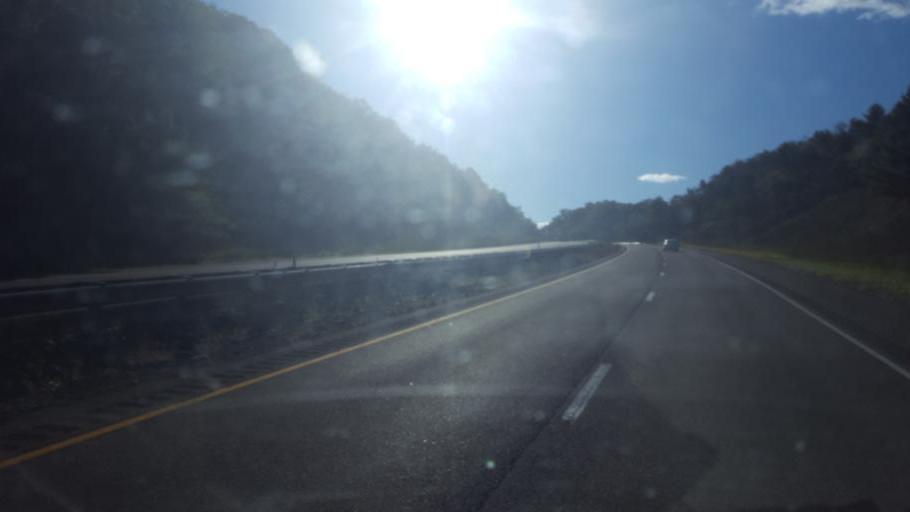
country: US
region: West Virginia
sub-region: Morgan County
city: Berkeley Springs
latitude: 39.6699
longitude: -78.4534
